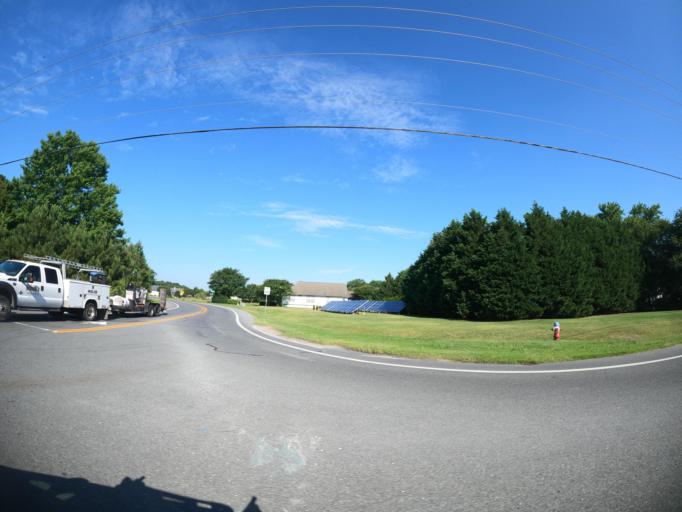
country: US
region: Delaware
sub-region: Sussex County
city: Ocean View
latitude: 38.5254
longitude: -75.0943
